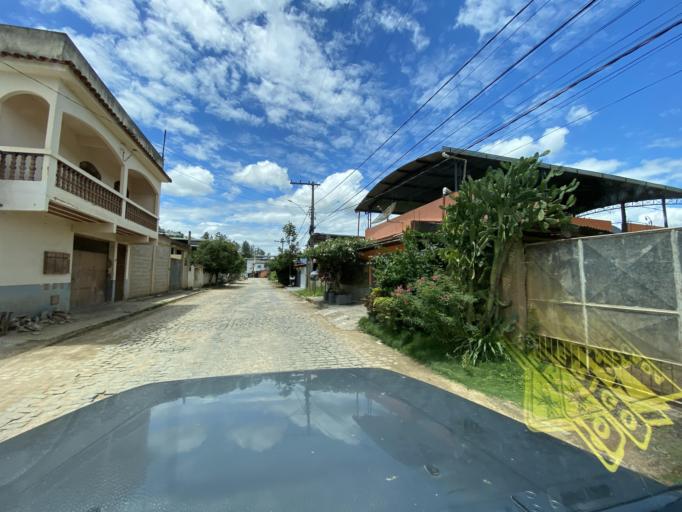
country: BR
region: Espirito Santo
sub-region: Jeronimo Monteiro
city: Jeronimo Monteiro
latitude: -20.7835
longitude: -41.3894
